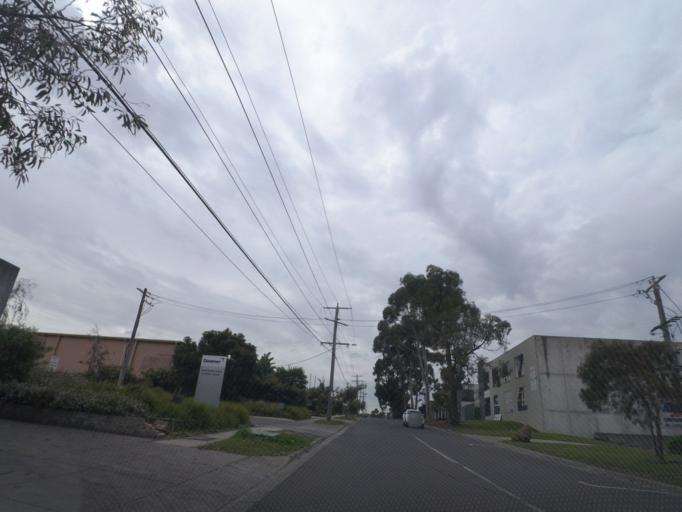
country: AU
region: Victoria
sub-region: Knox
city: Bayswater
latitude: -37.8407
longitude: 145.2796
